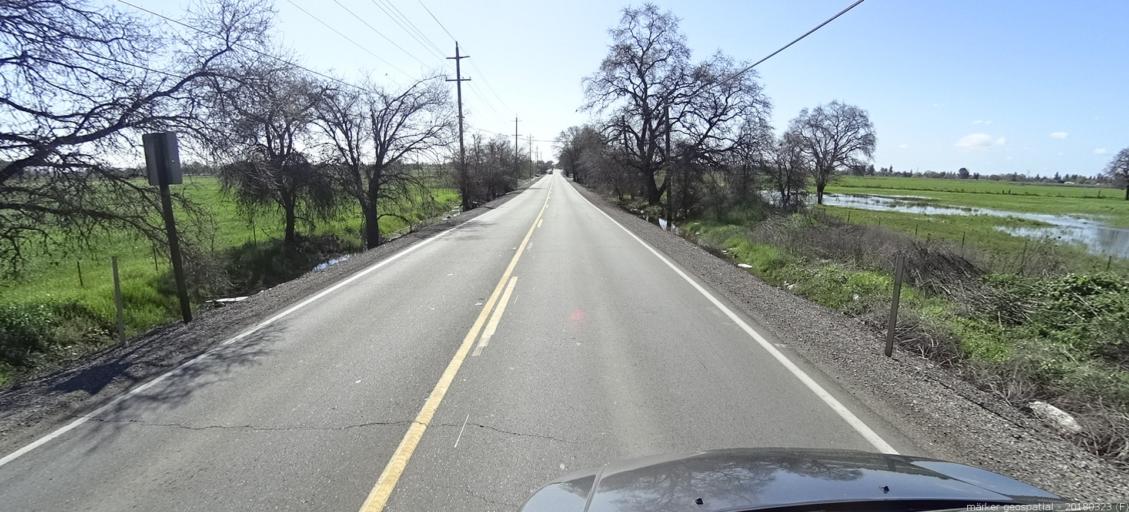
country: US
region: California
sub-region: Sacramento County
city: Rio Linda
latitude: 38.6708
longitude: -121.4545
